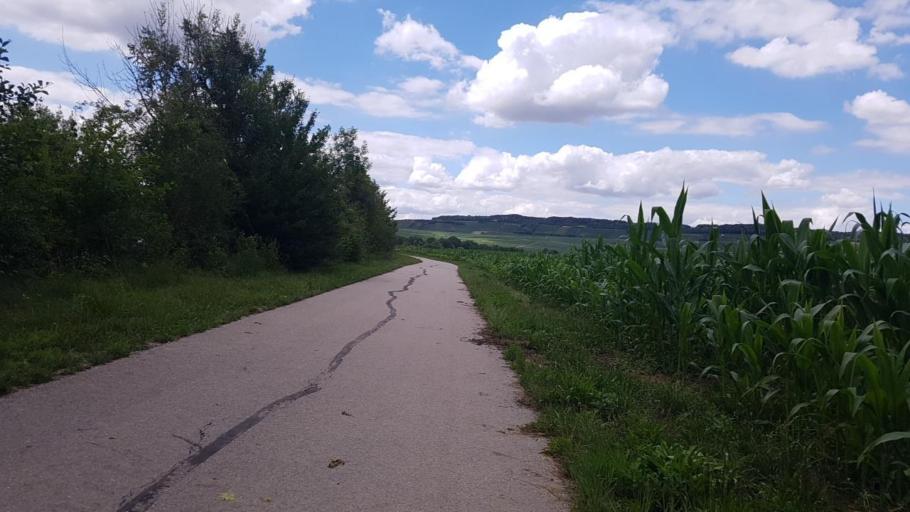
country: FR
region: Champagne-Ardenne
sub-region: Departement de la Marne
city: Chatillon-sur-Marne
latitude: 49.0947
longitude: 3.7382
